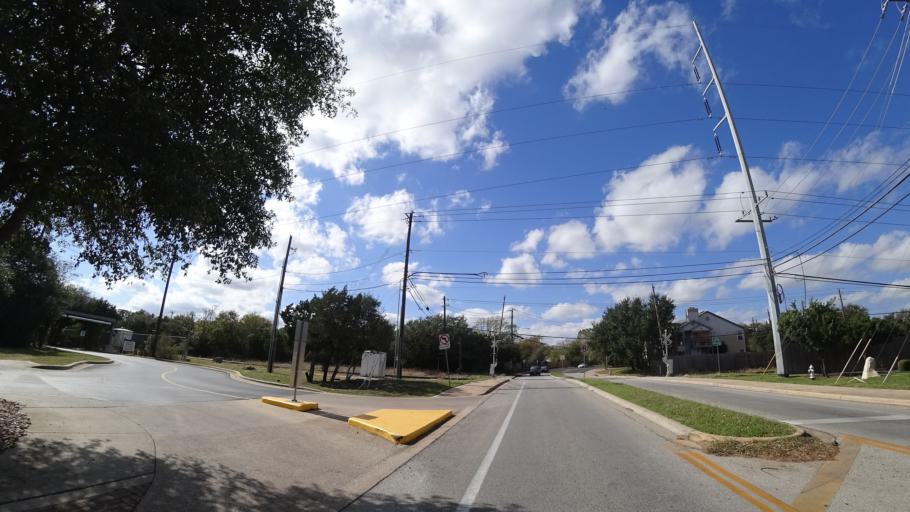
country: US
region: Texas
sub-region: Williamson County
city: Jollyville
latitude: 30.4116
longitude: -97.7288
